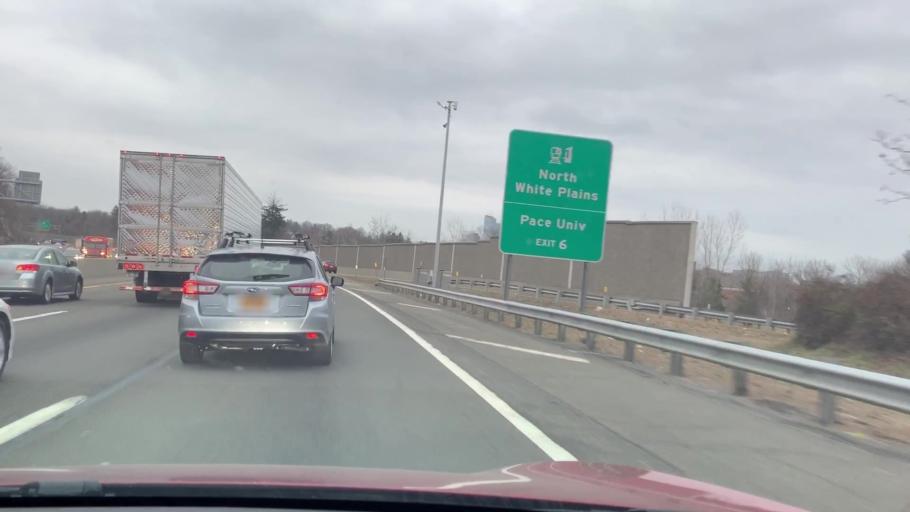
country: US
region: New York
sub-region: Westchester County
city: Fairview
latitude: 41.0426
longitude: -73.7865
